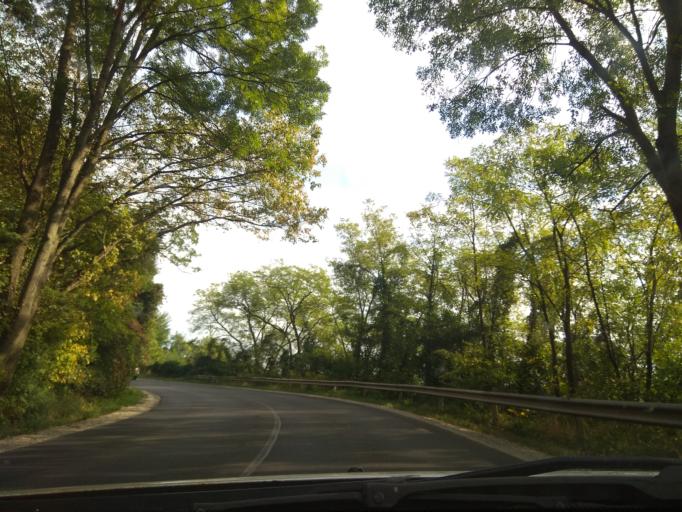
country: HU
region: Borsod-Abauj-Zemplen
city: Miskolc
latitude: 48.0878
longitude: 20.7513
